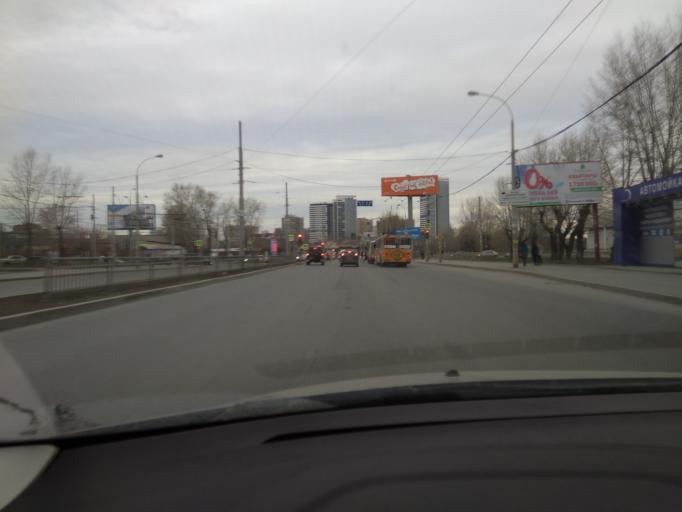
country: RU
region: Sverdlovsk
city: Yekaterinburg
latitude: 56.7915
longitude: 60.6441
